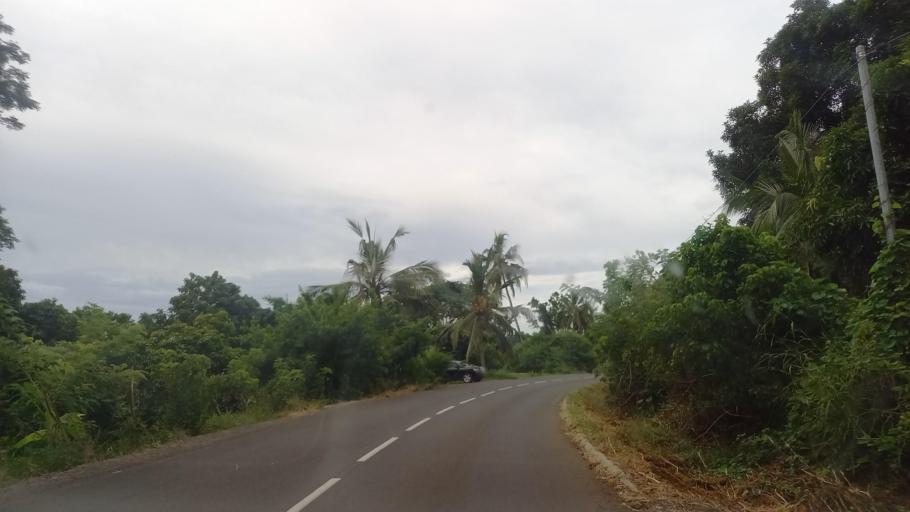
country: YT
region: Kani-Keli
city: Kani Keli
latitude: -12.9529
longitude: 45.0970
